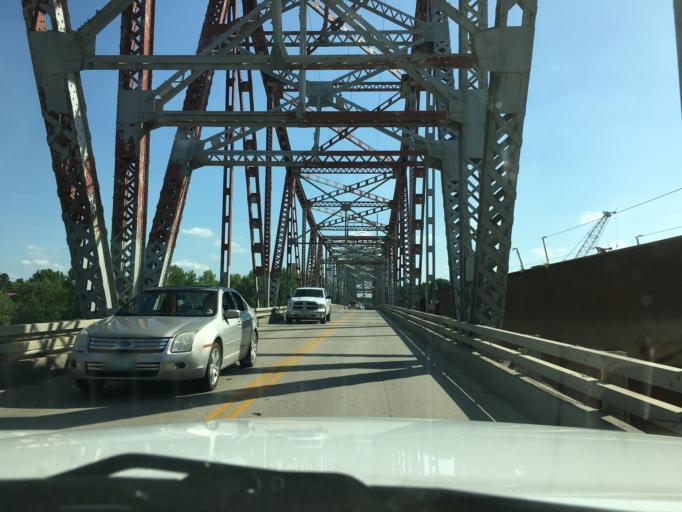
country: US
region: Missouri
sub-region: Franklin County
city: Washington
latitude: 38.5576
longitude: -90.9981
